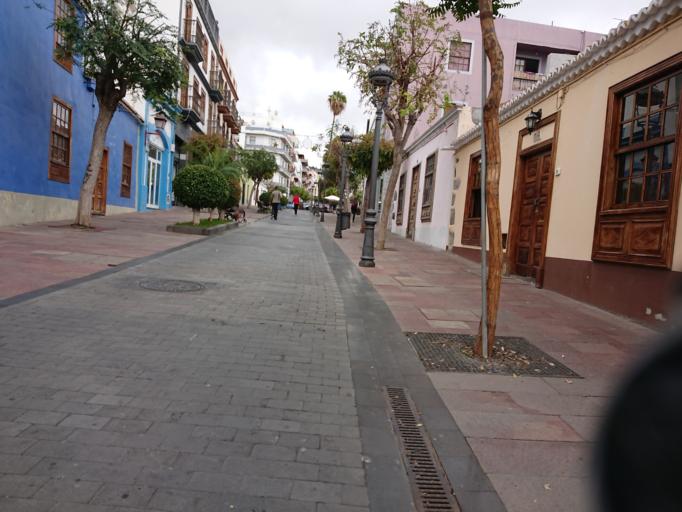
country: ES
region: Canary Islands
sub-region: Provincia de Santa Cruz de Tenerife
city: Los Llanos de Aridane
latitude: 28.6584
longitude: -17.9102
